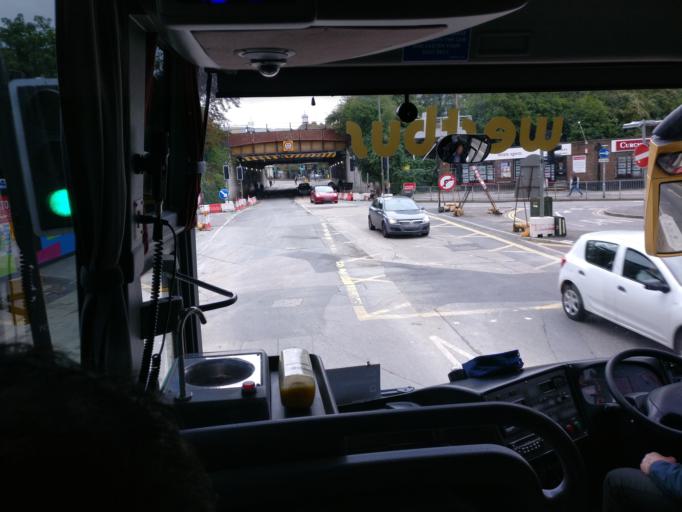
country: GB
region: England
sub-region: Surrey
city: Woking
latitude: 51.3179
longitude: -0.5608
